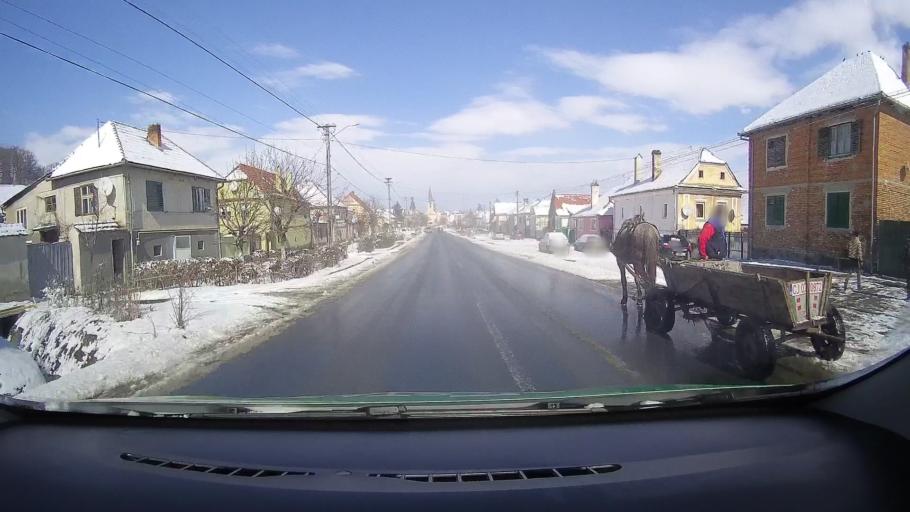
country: RO
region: Sibiu
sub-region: Comuna Nocrich
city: Nocrich
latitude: 45.8911
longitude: 24.4532
